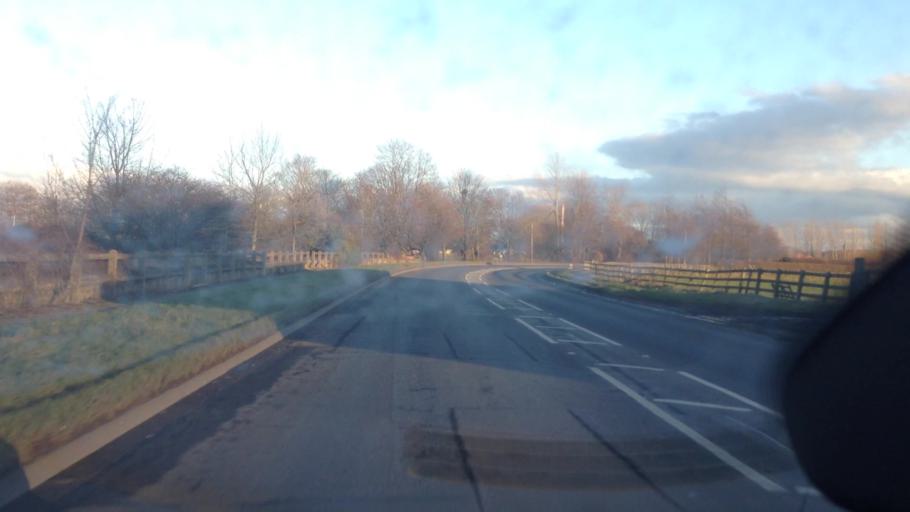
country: GB
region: England
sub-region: City and Borough of Leeds
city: Otley
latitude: 53.9098
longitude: -1.6642
